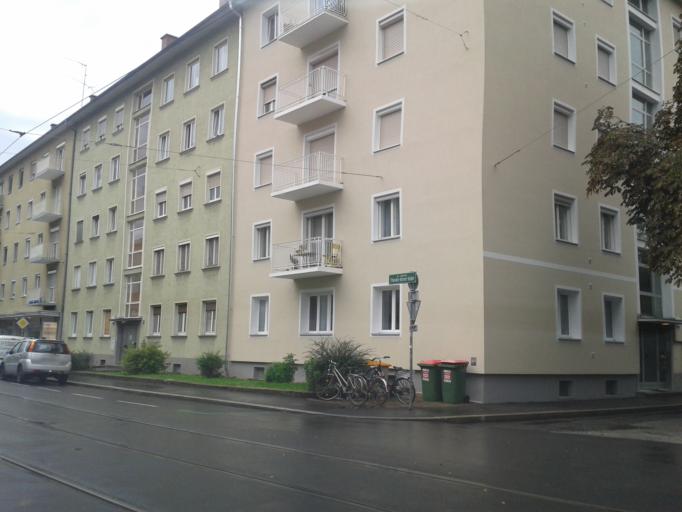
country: AT
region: Styria
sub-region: Graz Stadt
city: Goesting
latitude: 47.0937
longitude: 15.4235
